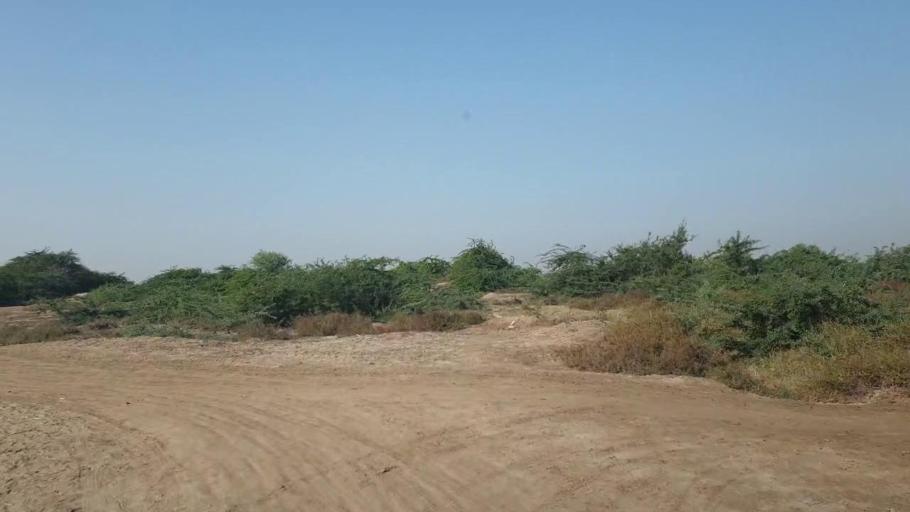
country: PK
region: Sindh
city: Badin
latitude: 24.4537
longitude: 68.7233
